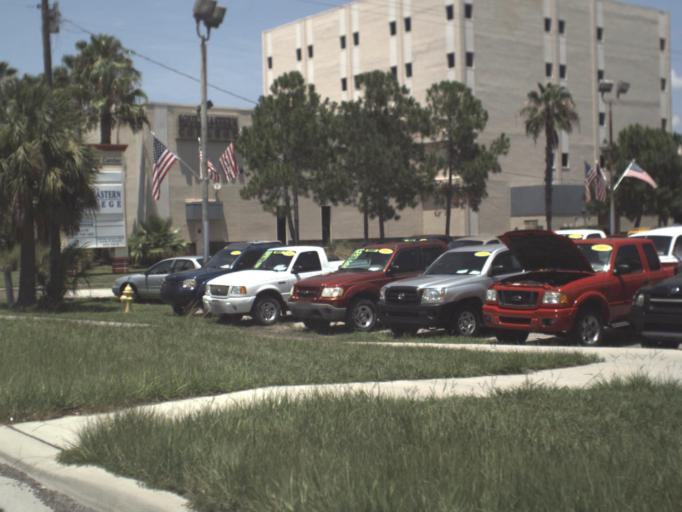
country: US
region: Florida
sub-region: Pasco County
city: New Port Richey
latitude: 28.2458
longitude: -82.7276
